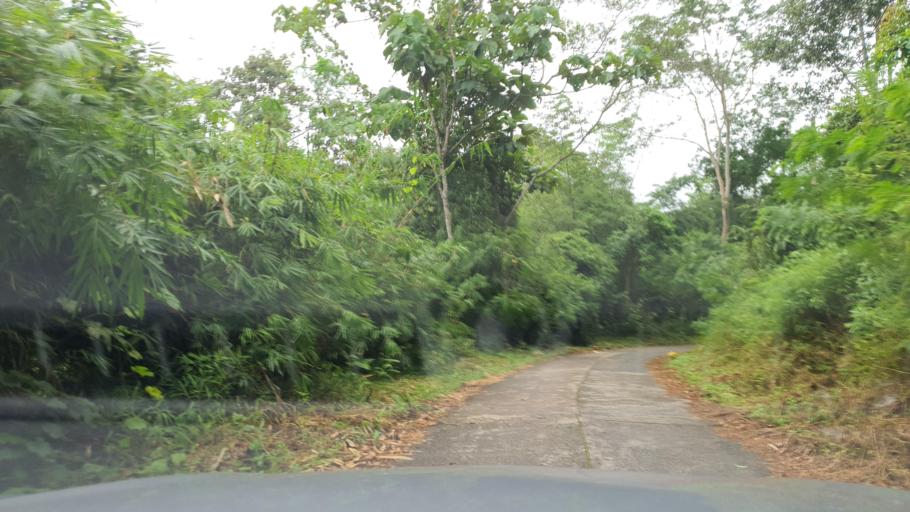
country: TH
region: Chiang Mai
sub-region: Amphoe Chiang Dao
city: Chiang Dao
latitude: 19.2713
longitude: 98.9393
